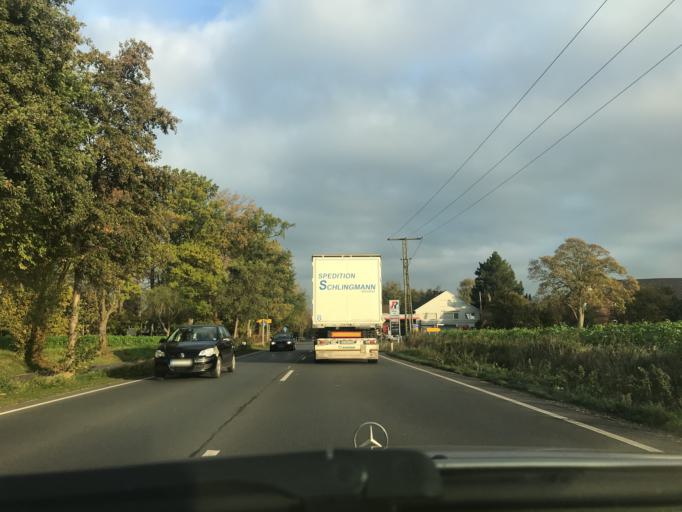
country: DE
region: North Rhine-Westphalia
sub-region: Regierungsbezirk Arnsberg
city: Soest
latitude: 51.6288
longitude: 8.1001
